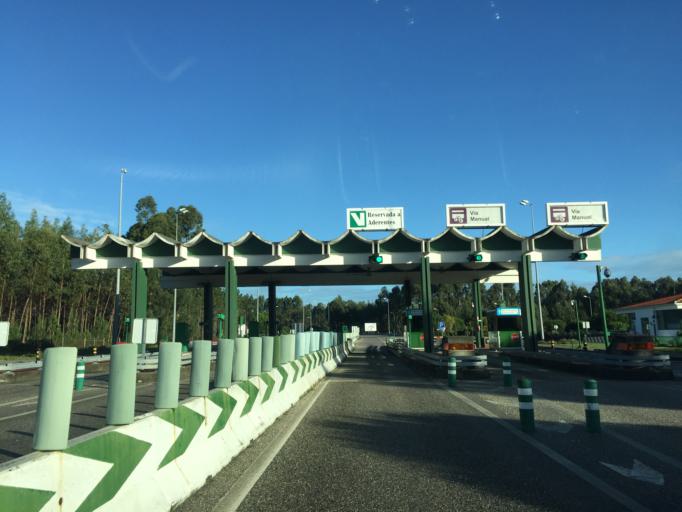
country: PT
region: Coimbra
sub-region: Figueira da Foz
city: Lavos
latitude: 40.0471
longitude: -8.8145
